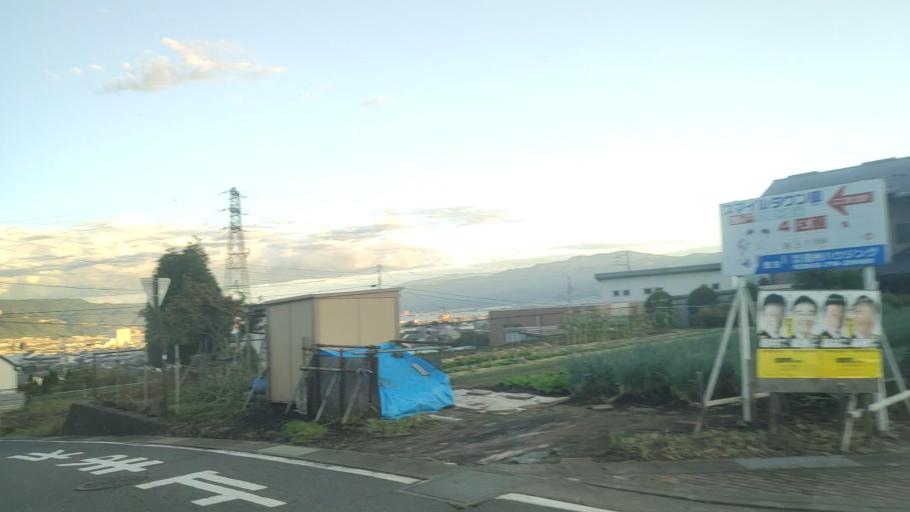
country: JP
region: Nagano
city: Okaya
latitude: 36.0846
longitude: 138.0659
